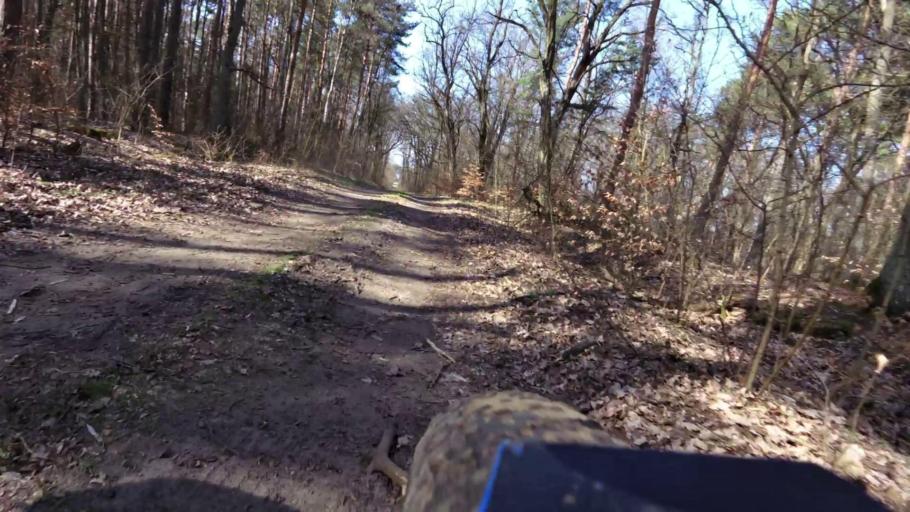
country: PL
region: Lubusz
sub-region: Powiat slubicki
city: Cybinka
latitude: 52.2177
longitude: 14.8489
